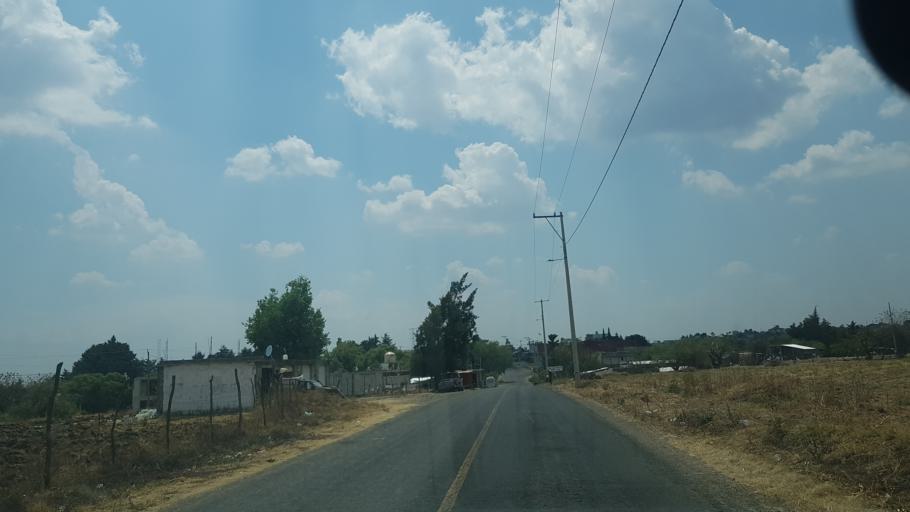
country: MX
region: Puebla
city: San Juan Amecac
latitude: 18.8279
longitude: -98.6524
